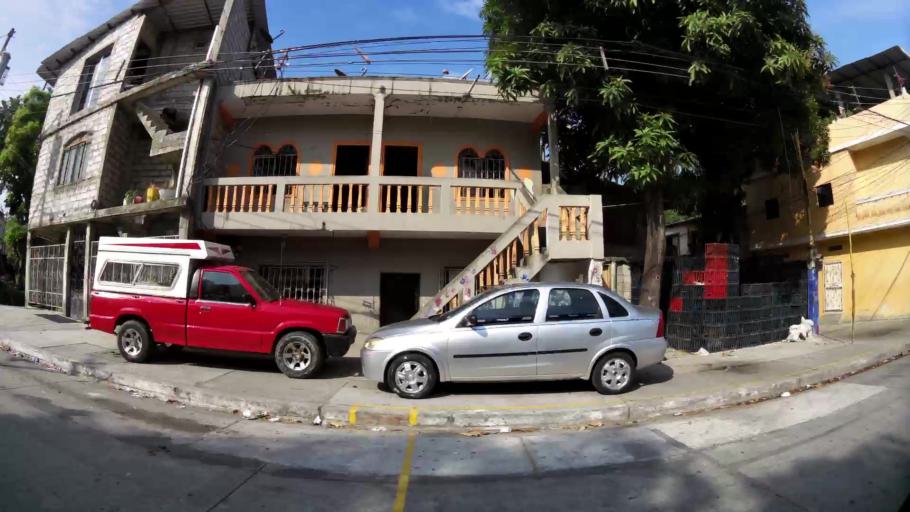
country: EC
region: Guayas
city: Guayaquil
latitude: -2.1840
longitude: -79.9039
